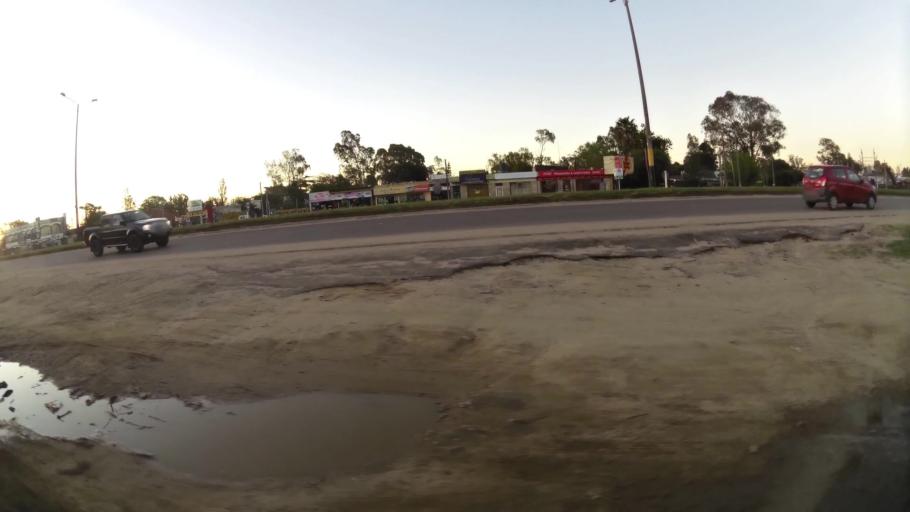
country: UY
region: Canelones
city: Colonia Nicolich
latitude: -34.8253
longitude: -55.9639
